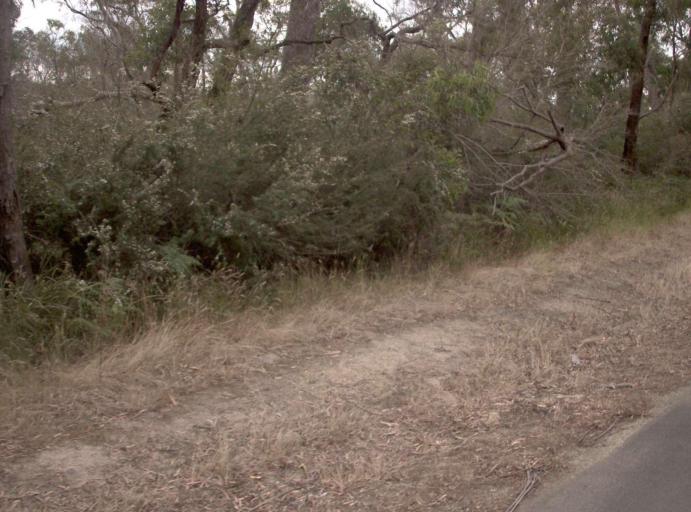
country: AU
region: Victoria
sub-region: Wellington
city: Sale
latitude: -38.2132
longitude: 147.0634
